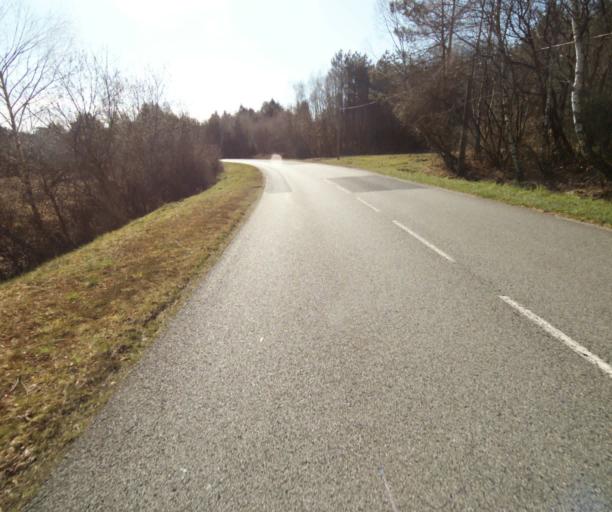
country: FR
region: Limousin
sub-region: Departement de la Correze
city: Correze
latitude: 45.2812
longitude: 1.9250
